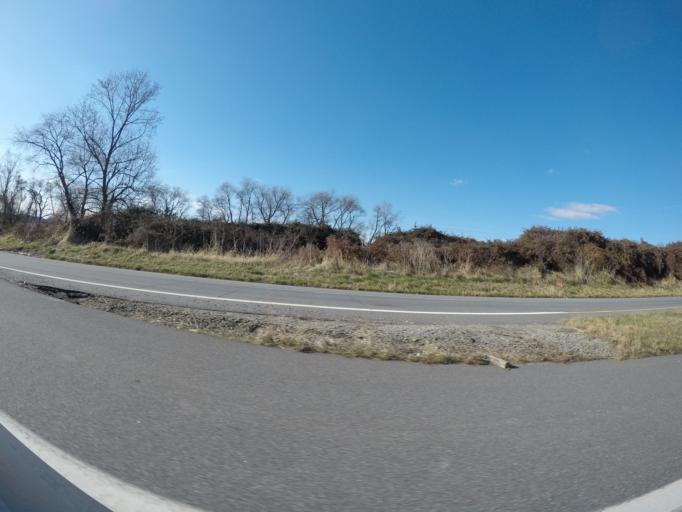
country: US
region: Pennsylvania
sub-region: Chester County
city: Oxford
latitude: 39.7863
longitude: -75.9980
